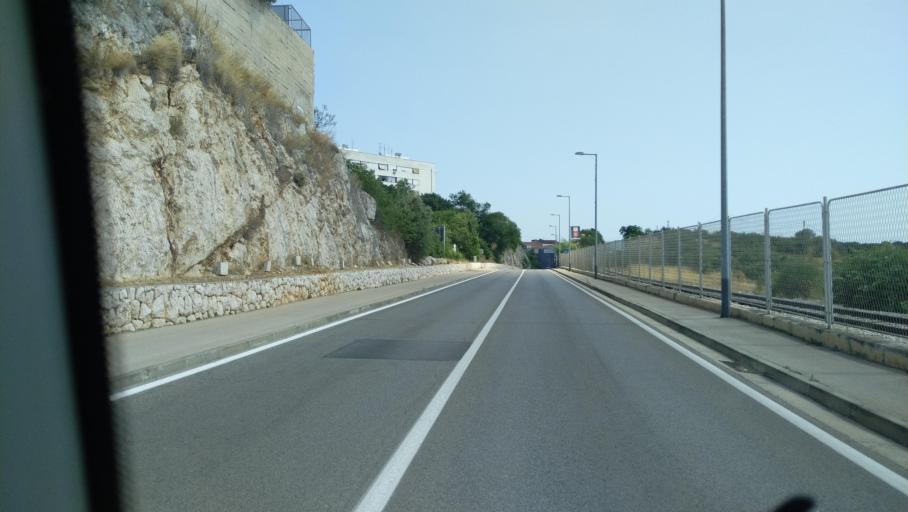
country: HR
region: Sibensko-Kniniska
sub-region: Grad Sibenik
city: Sibenik
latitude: 43.7271
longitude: 15.9032
